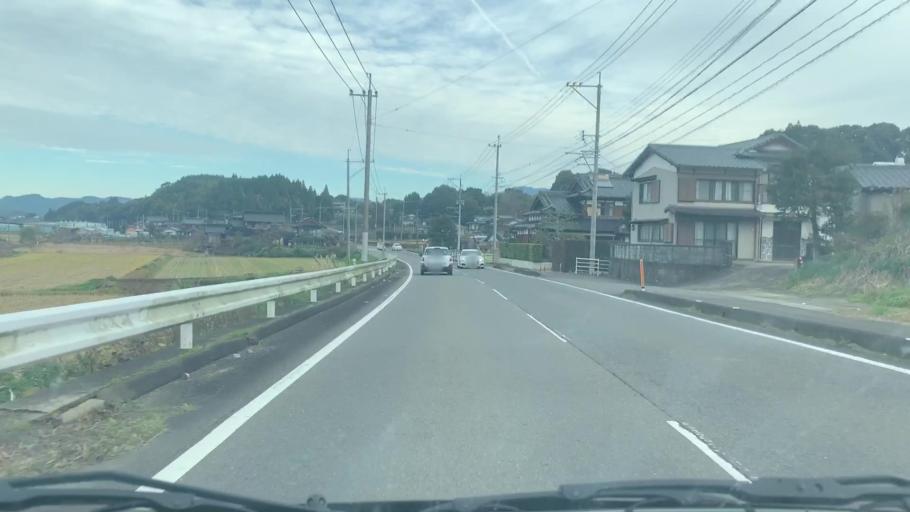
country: JP
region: Saga Prefecture
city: Imaricho-ko
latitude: 33.2816
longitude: 129.9680
